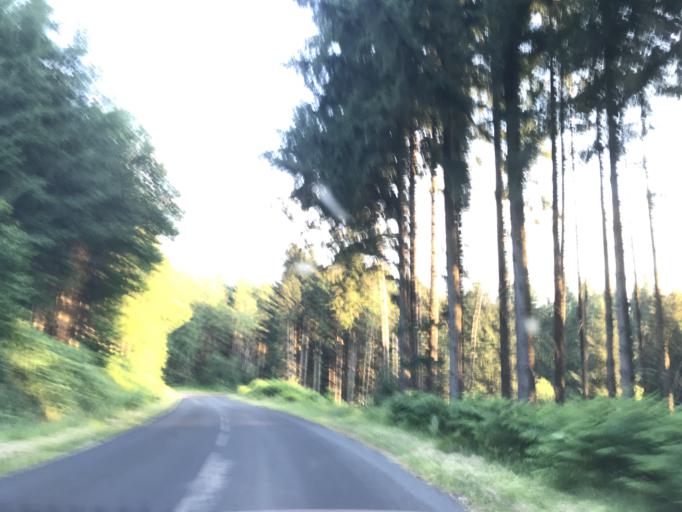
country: FR
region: Auvergne
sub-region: Departement du Puy-de-Dome
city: Celles-sur-Durolle
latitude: 45.7569
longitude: 3.6649
